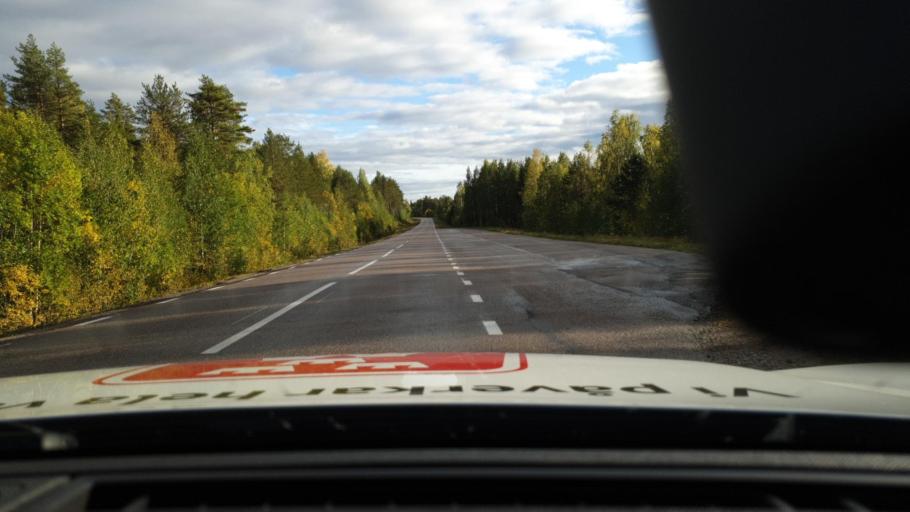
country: SE
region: Norrbotten
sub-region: Overkalix Kommun
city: OEverkalix
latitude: 66.6472
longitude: 22.7207
